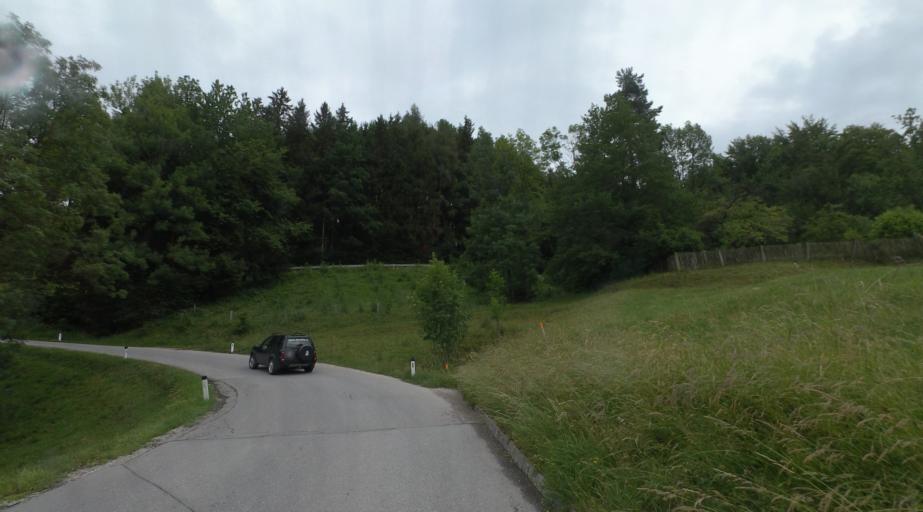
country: AT
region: Upper Austria
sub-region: Politischer Bezirk Kirchdorf an der Krems
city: Micheldorf in Oberoesterreich
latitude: 47.9139
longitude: 14.1451
